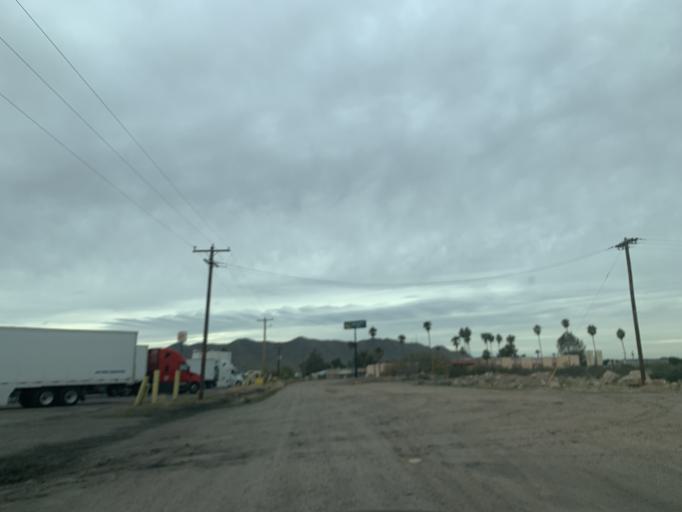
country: US
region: Arizona
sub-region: Pinal County
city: Arizona City
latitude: 32.8140
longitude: -111.6693
